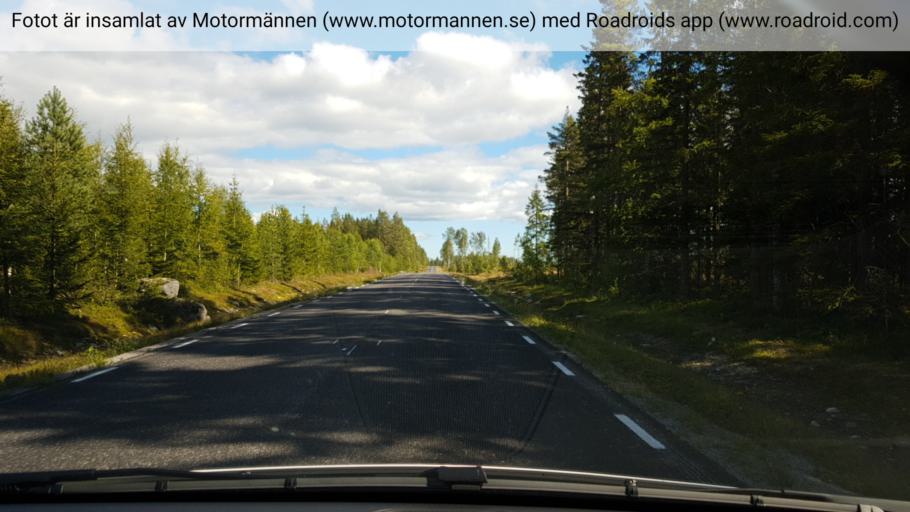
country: SE
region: Vaesterbotten
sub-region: Umea Kommun
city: Hoernefors
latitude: 63.6988
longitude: 19.7427
